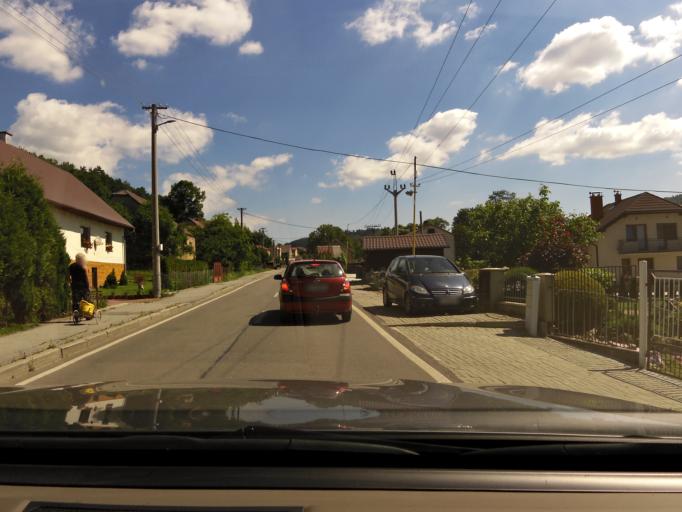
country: PL
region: Silesian Voivodeship
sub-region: Powiat cieszynski
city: Koniakow
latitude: 49.4980
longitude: 18.9361
